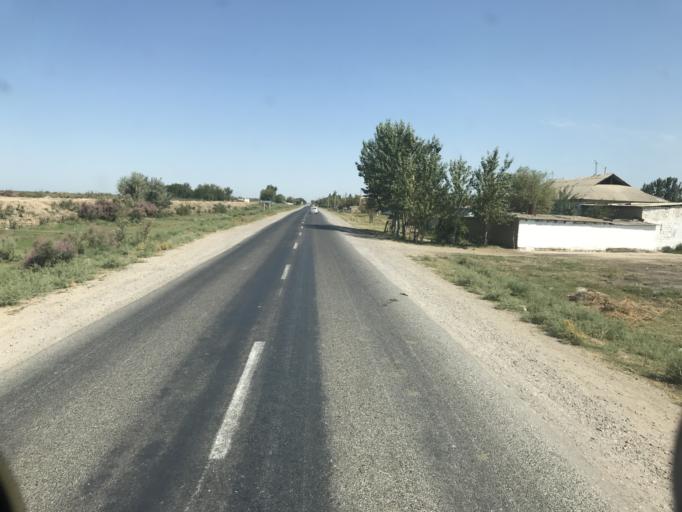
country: KZ
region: Ongtustik Qazaqstan
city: Myrzakent
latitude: 40.7551
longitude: 68.5370
